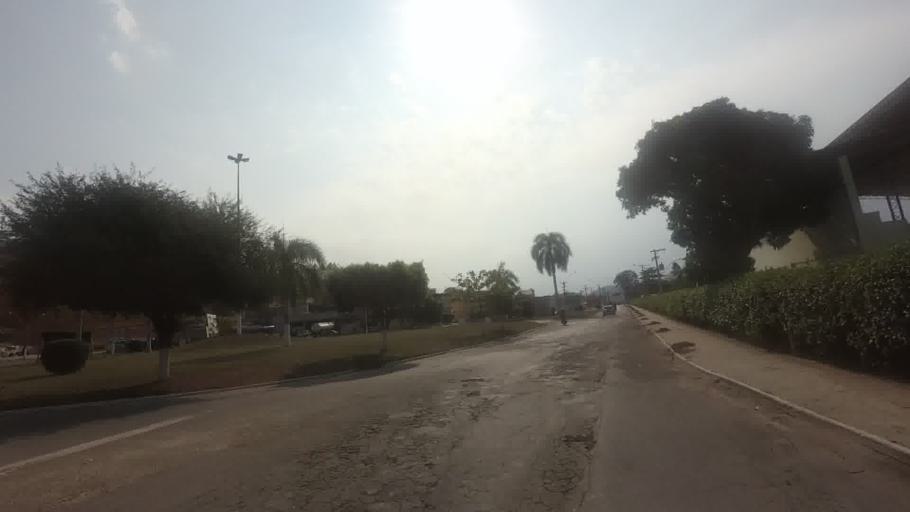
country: BR
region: Rio de Janeiro
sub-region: Bom Jesus Do Itabapoana
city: Bom Jesus do Itabapoana
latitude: -21.1351
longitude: -41.6619
